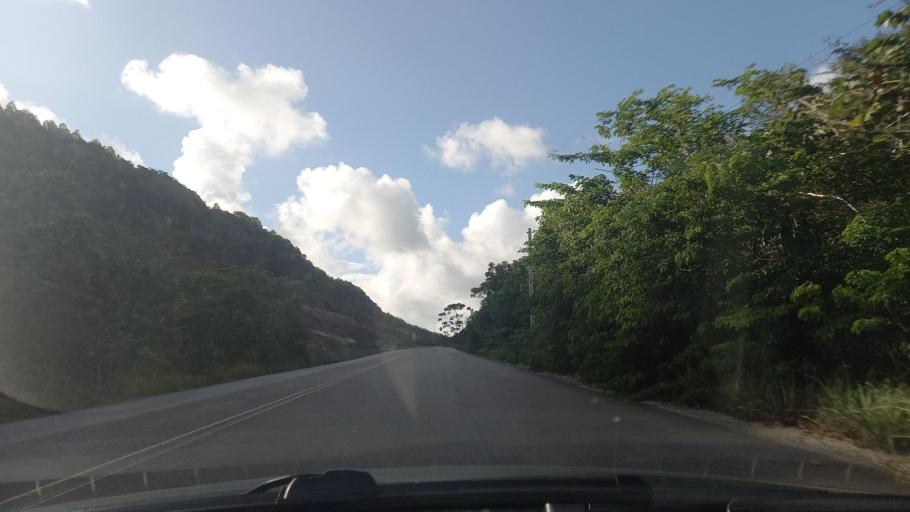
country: BR
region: Alagoas
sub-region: Marechal Deodoro
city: Marechal Deodoro
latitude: -9.8352
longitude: -35.9292
